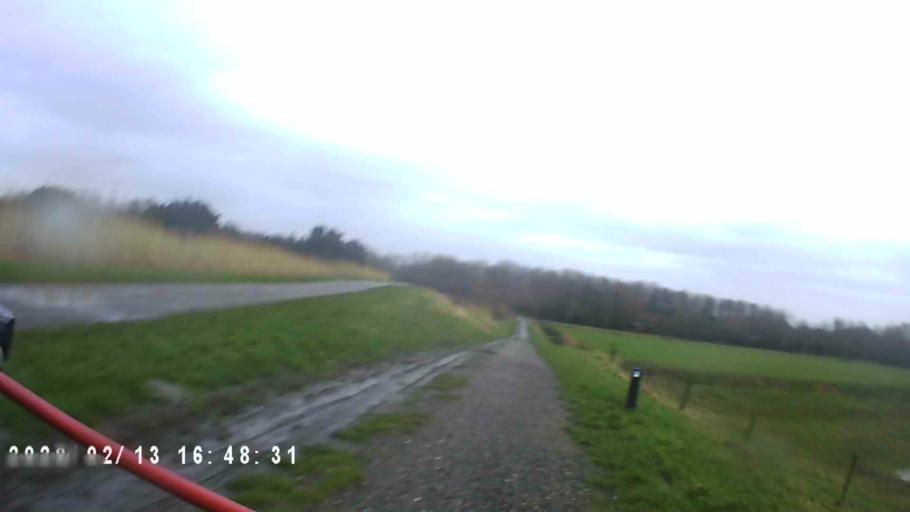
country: NL
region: Groningen
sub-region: Gemeente Groningen
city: Groningen
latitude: 53.2170
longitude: 6.5188
